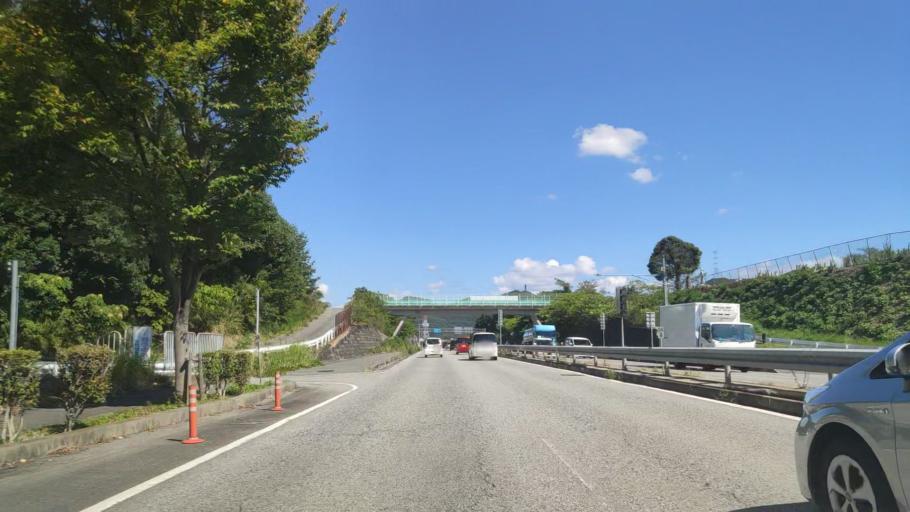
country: JP
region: Hyogo
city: Yashiro
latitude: 34.9462
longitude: 134.9688
